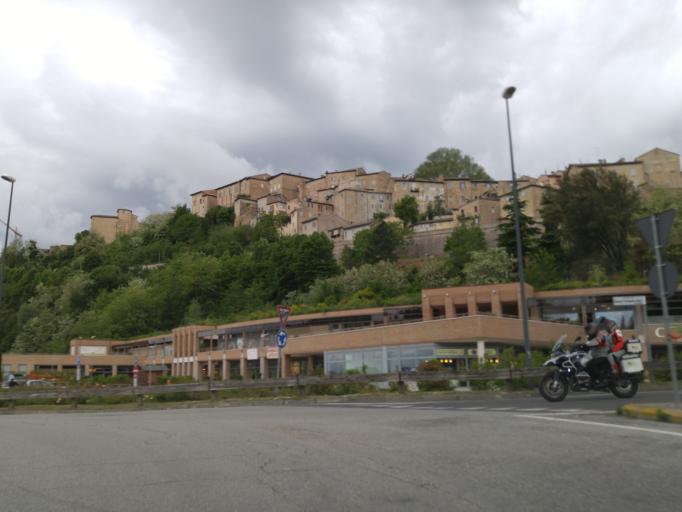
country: IT
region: The Marches
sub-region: Provincia di Pesaro e Urbino
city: Urbino
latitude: 43.7260
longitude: 12.6409
